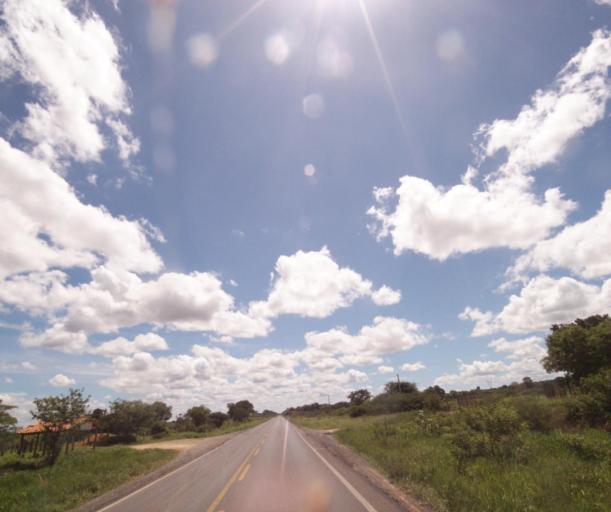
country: BR
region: Bahia
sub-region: Sao Felix Do Coribe
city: Santa Maria da Vitoria
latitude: -13.3917
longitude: -44.1156
